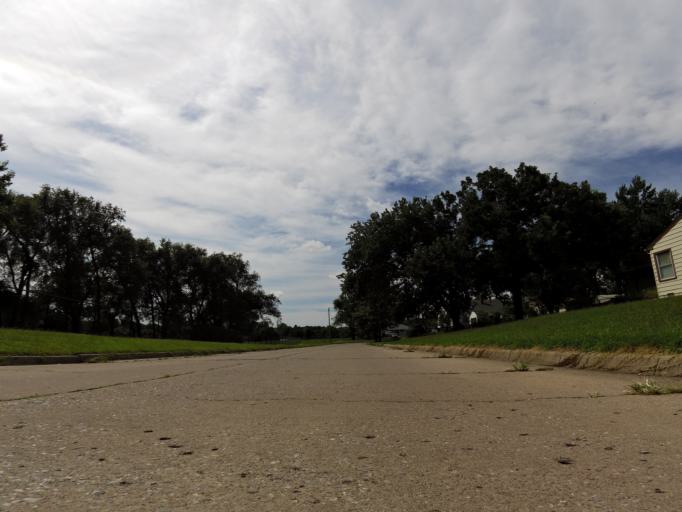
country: US
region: Kansas
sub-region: Sedgwick County
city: Wichita
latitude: 37.7001
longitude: -97.2917
